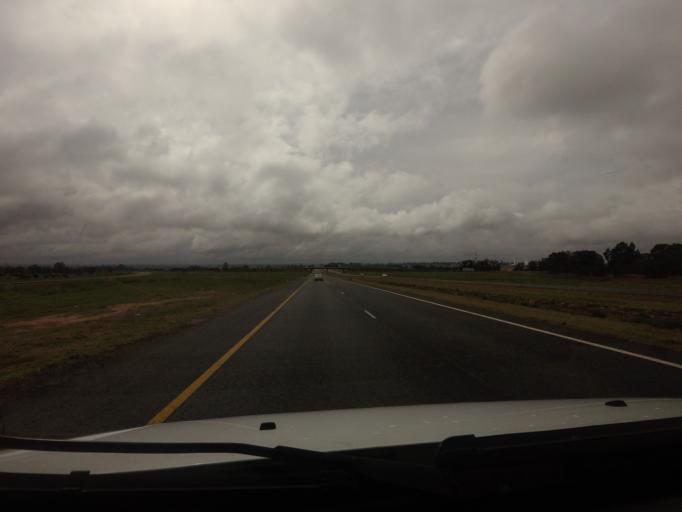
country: ZA
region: Mpumalanga
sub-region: Nkangala District Municipality
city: Witbank
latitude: -25.8701
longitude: 29.0738
